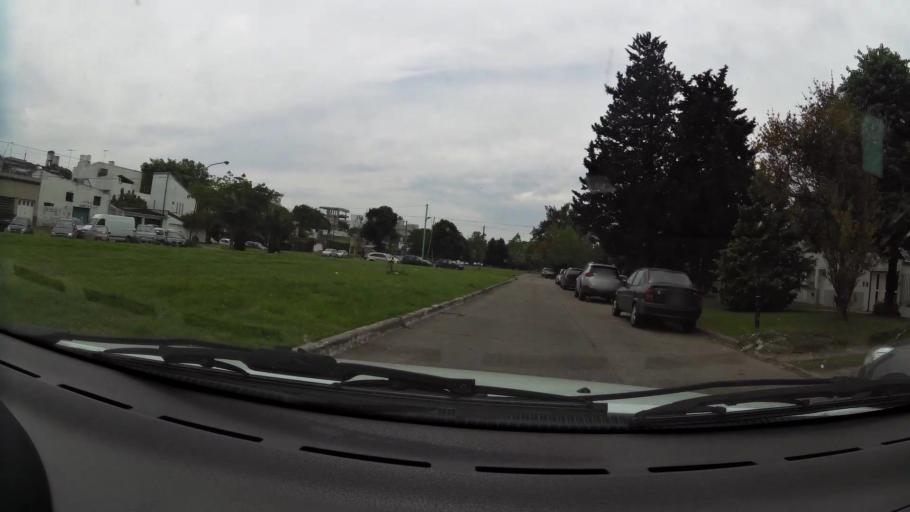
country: AR
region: Buenos Aires
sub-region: Partido de La Plata
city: La Plata
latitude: -34.9368
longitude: -57.9713
